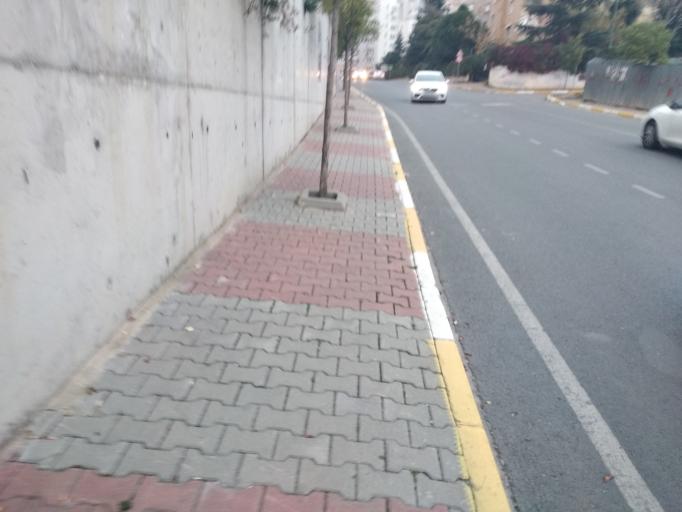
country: TR
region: Istanbul
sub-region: Atasehir
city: Atasehir
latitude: 40.9850
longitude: 29.1214
